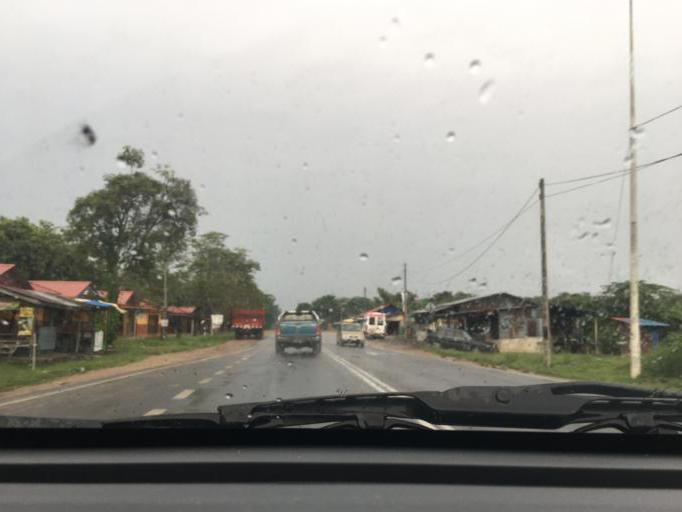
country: MY
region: Kedah
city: Sungai Petani
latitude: 5.5940
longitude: 100.6395
